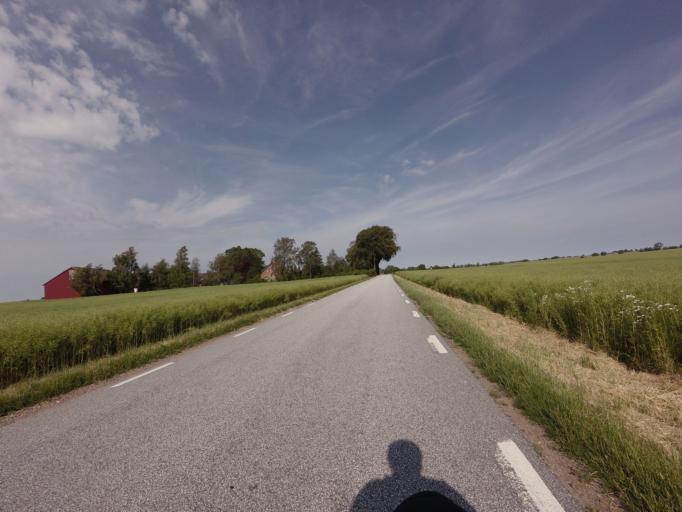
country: SE
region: Skane
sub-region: Vellinge Kommun
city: Vellinge
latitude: 55.5002
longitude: 13.0452
